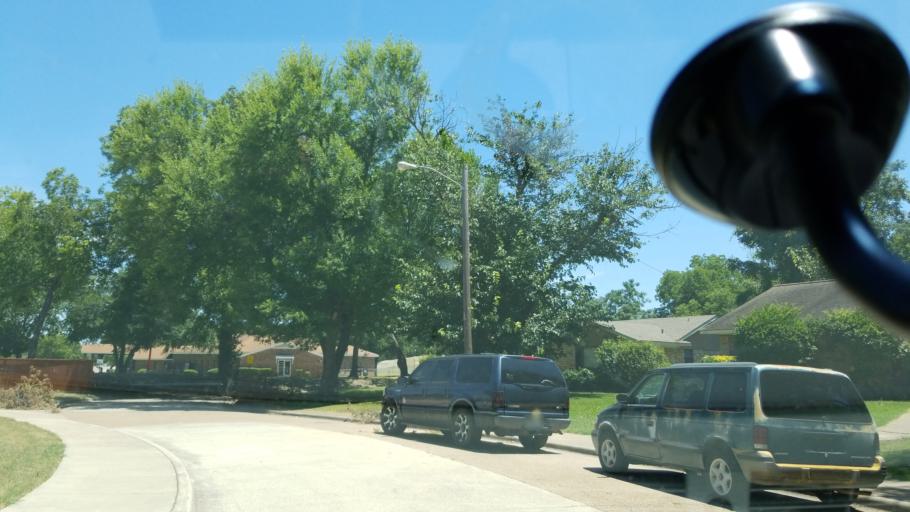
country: US
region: Texas
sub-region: Dallas County
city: Cockrell Hill
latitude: 32.6896
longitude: -96.8320
